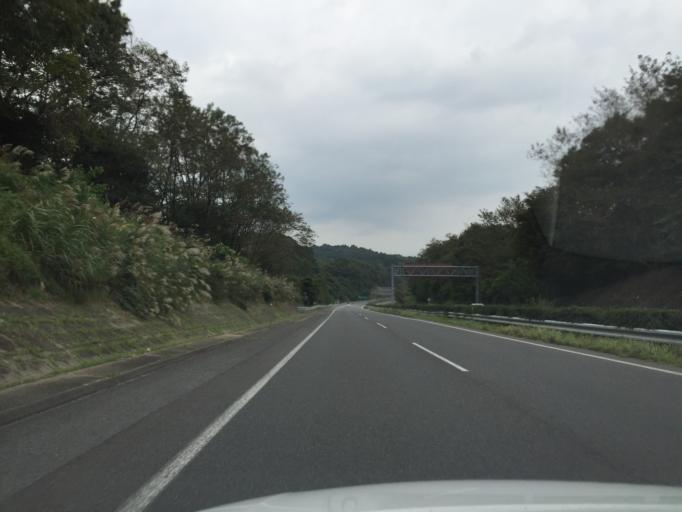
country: JP
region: Fukushima
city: Iwaki
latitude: 37.0449
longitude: 140.8207
